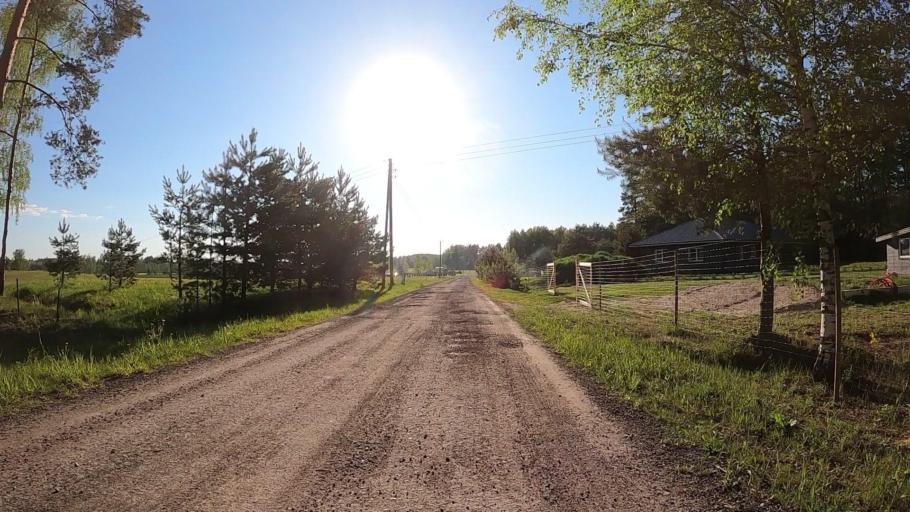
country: LV
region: Baldone
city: Baldone
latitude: 56.7738
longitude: 24.3175
